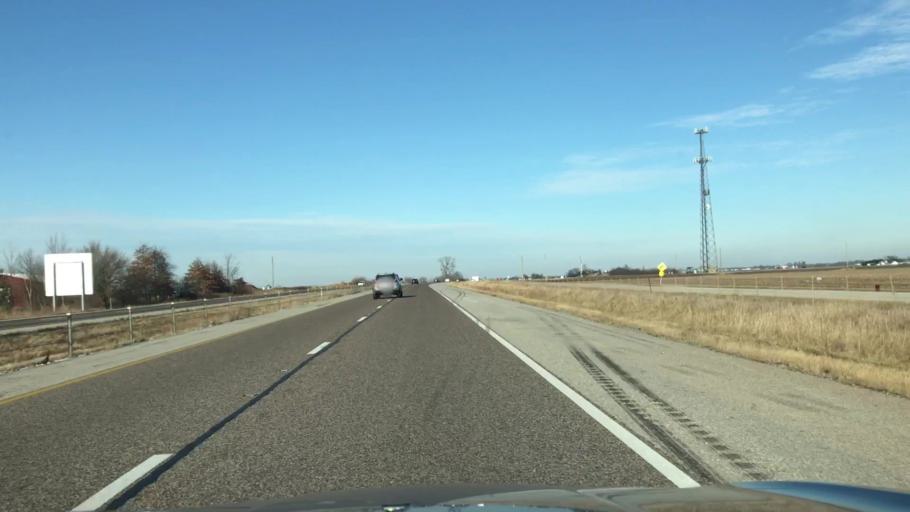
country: US
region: Illinois
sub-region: Madison County
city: Edwardsville
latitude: 38.8120
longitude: -89.8906
